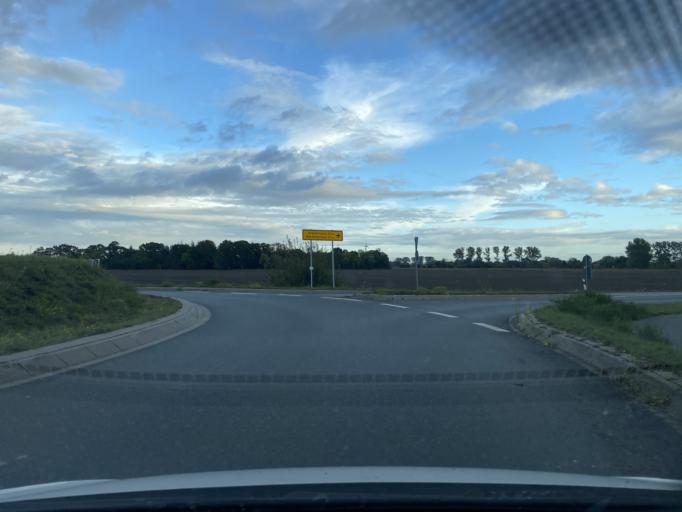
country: DE
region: Lower Saxony
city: Otterndorf
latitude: 53.7959
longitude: 8.8926
